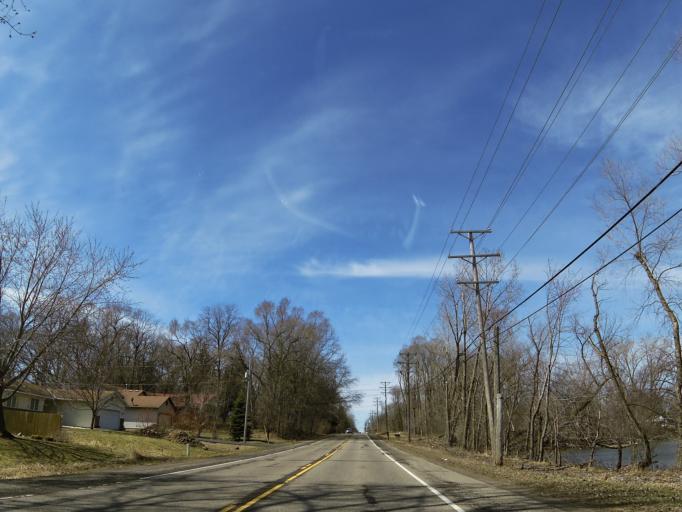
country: US
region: Minnesota
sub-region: Ramsey County
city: North Saint Paul
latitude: 44.9923
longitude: -92.9950
